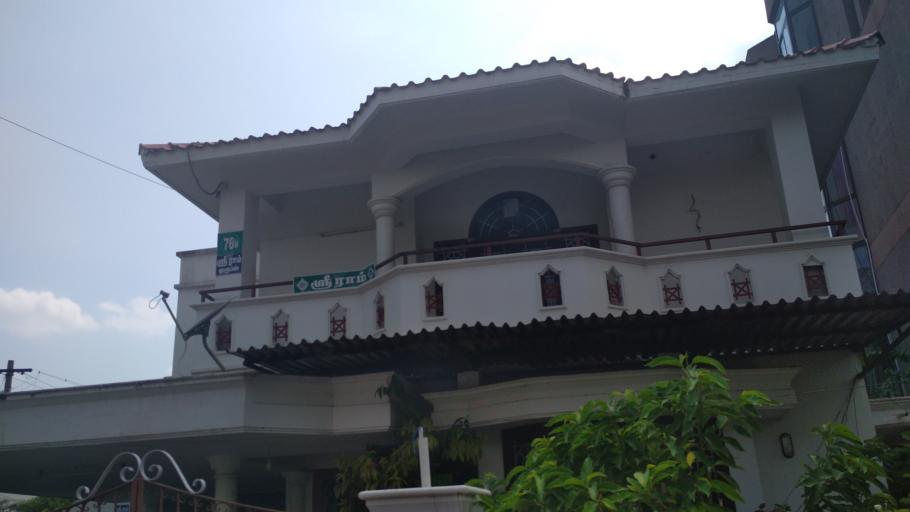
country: IN
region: Tamil Nadu
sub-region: Coimbatore
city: Coimbatore
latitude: 11.0249
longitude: 76.9394
